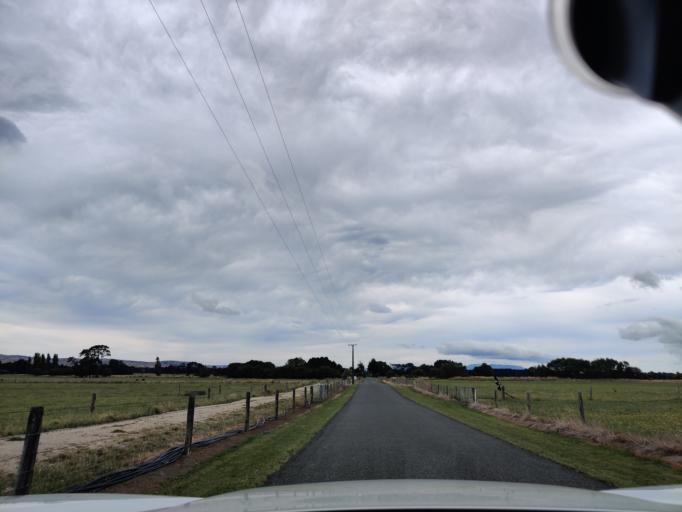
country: NZ
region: Wellington
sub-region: Masterton District
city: Masterton
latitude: -41.0307
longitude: 175.4462
